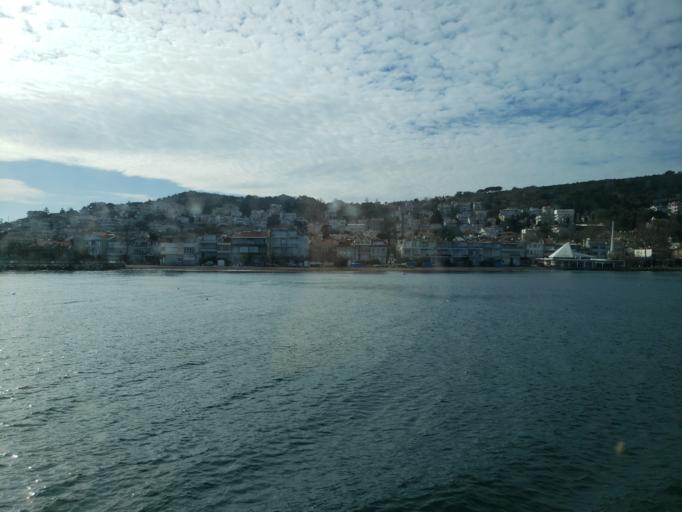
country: TR
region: Istanbul
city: Kinali
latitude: 40.9084
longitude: 29.0583
